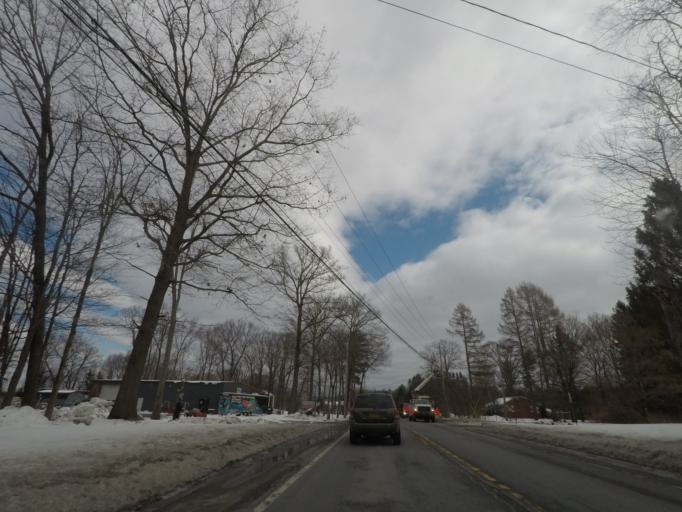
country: US
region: New York
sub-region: Washington County
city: Greenwich
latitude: 43.0931
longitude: -73.5347
